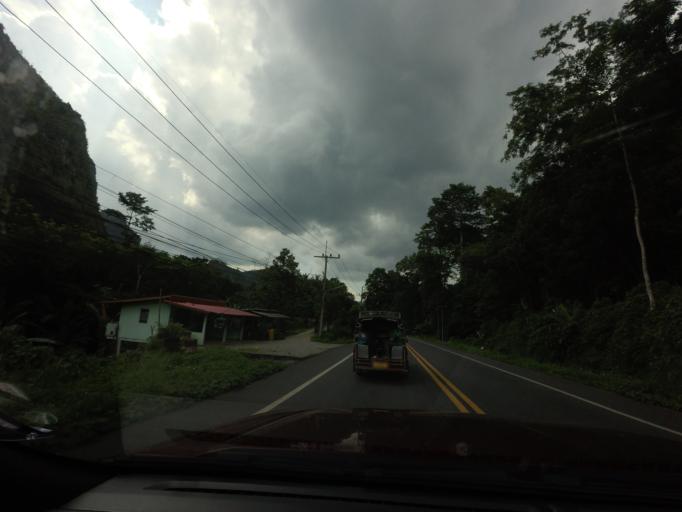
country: TH
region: Yala
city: Than To
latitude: 6.2131
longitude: 101.1665
